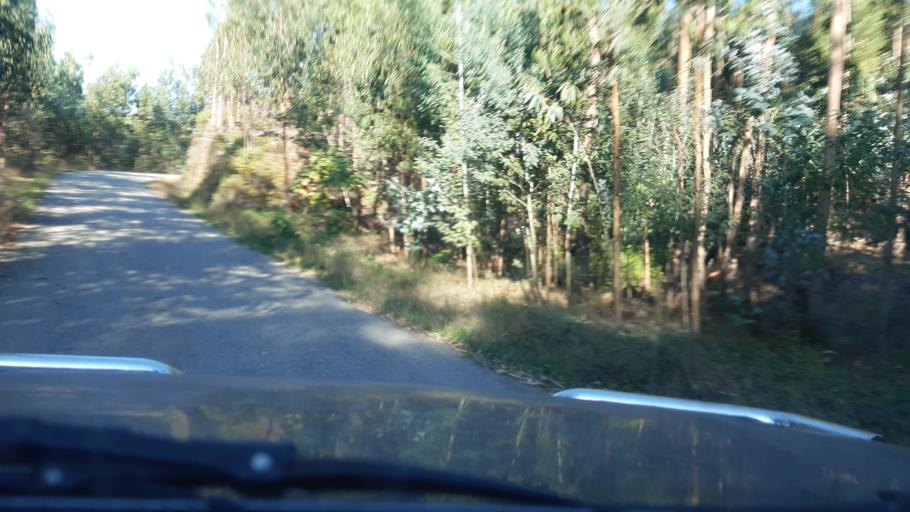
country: PT
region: Aveiro
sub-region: Agueda
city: Aguada de Cima
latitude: 40.5628
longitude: -8.3467
